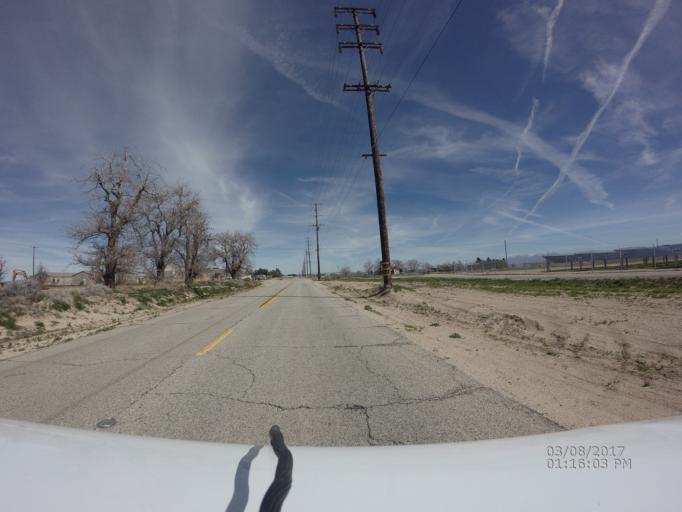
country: US
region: California
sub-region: Los Angeles County
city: Quartz Hill
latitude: 34.7185
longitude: -118.2727
